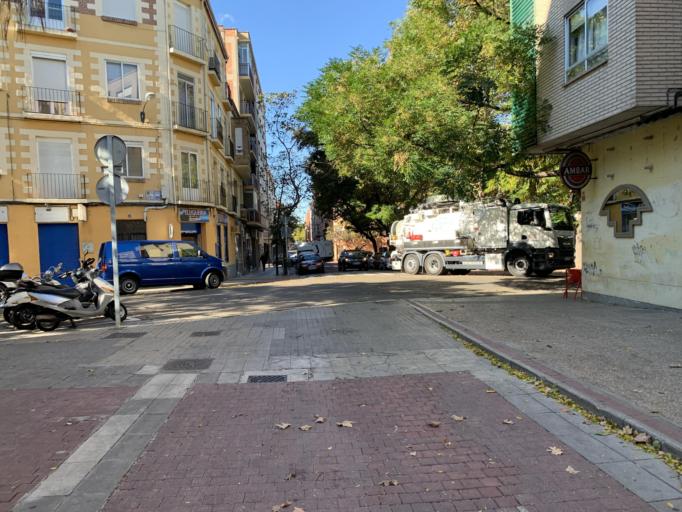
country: ES
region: Aragon
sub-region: Provincia de Zaragoza
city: Zaragoza
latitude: 41.6606
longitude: -0.8759
